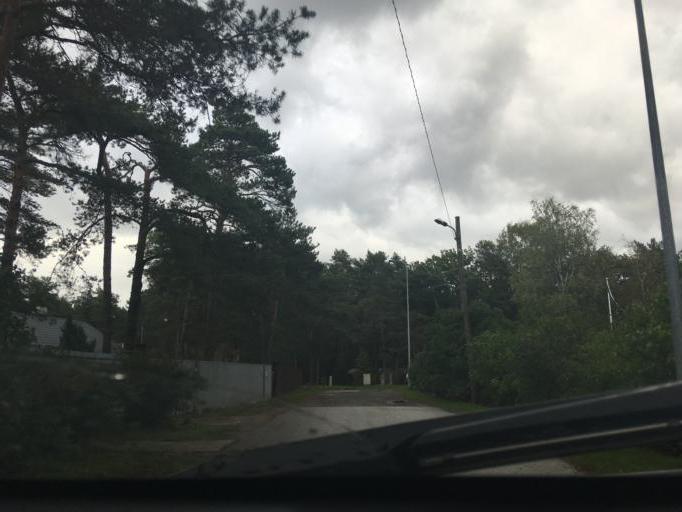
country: EE
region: Harju
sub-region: Saue vald
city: Laagri
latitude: 59.3637
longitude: 24.6486
